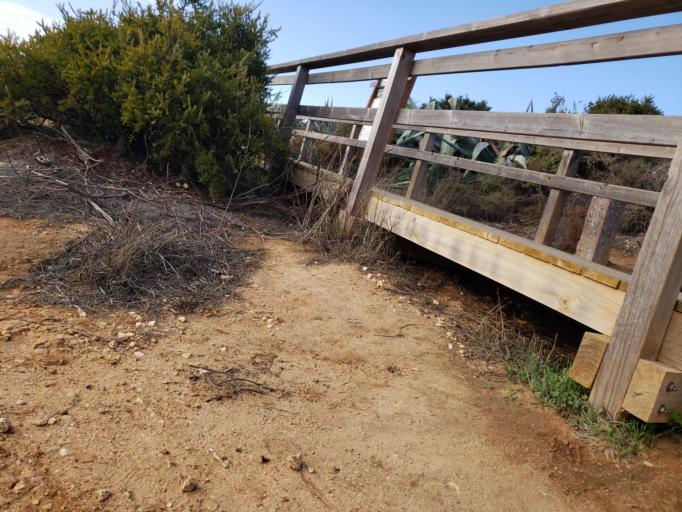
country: PT
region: Faro
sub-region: Lagos
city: Lagos
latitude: 37.0806
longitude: -8.6700
